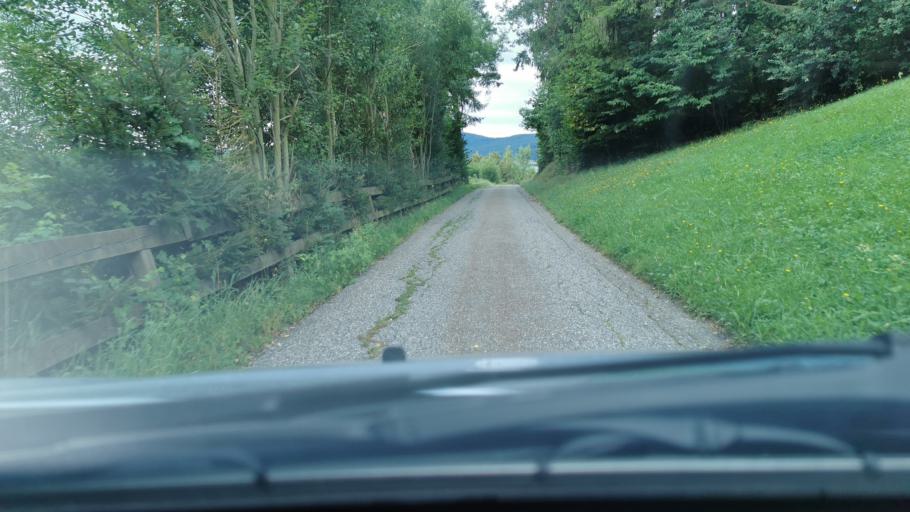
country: AT
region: Styria
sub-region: Politischer Bezirk Weiz
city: Birkfeld
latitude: 47.3593
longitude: 15.6958
